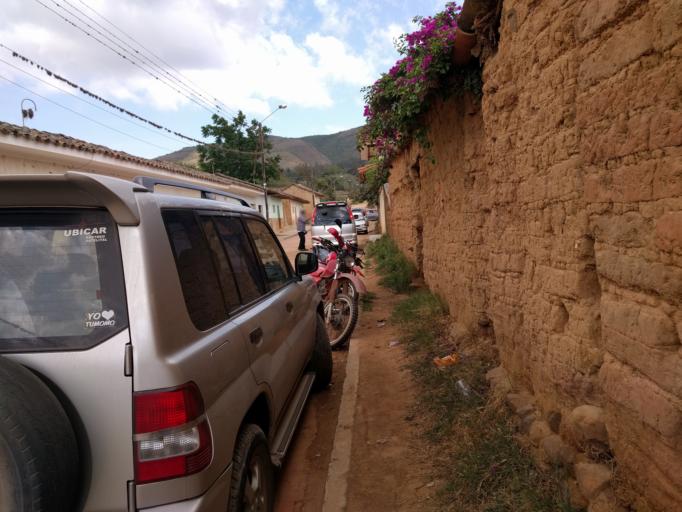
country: BO
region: Santa Cruz
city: Samaipata
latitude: -18.1814
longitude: -63.8759
